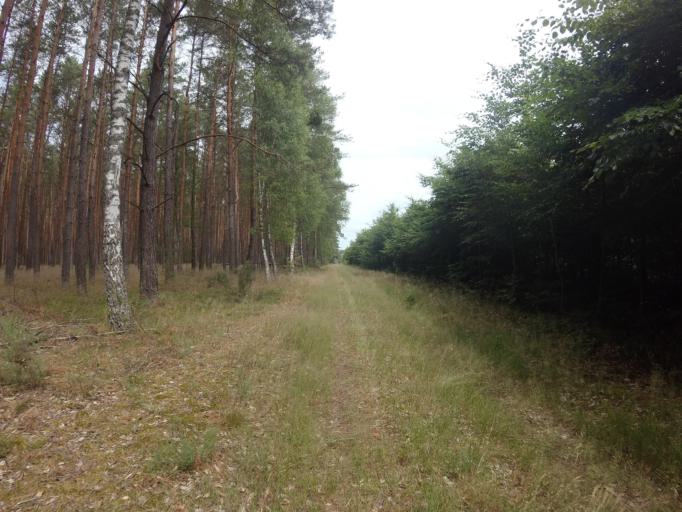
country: PL
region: West Pomeranian Voivodeship
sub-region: Powiat choszczenski
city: Bierzwnik
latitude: 53.1110
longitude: 15.6745
